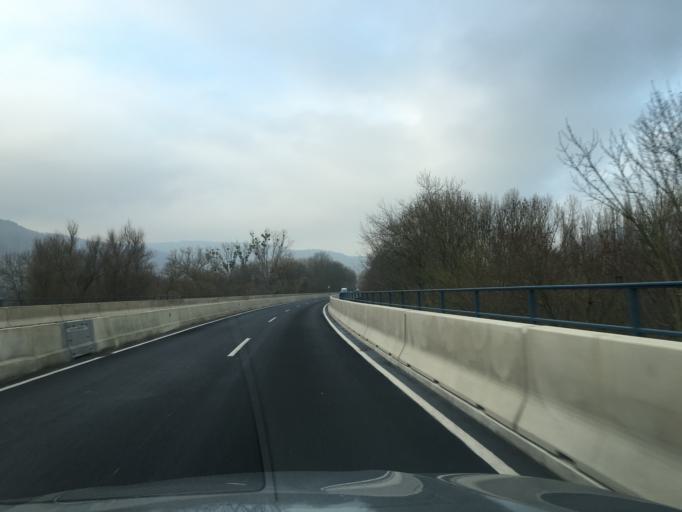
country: DE
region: Rheinland-Pfalz
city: Leutesdorf
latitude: 50.4471
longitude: 7.3796
